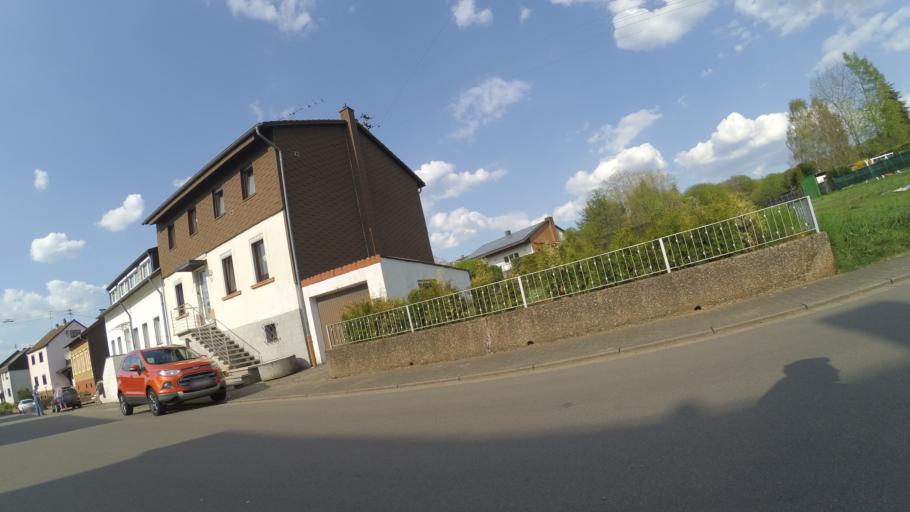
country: DE
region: Saarland
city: Riegelsberg
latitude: 49.3089
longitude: 6.9471
